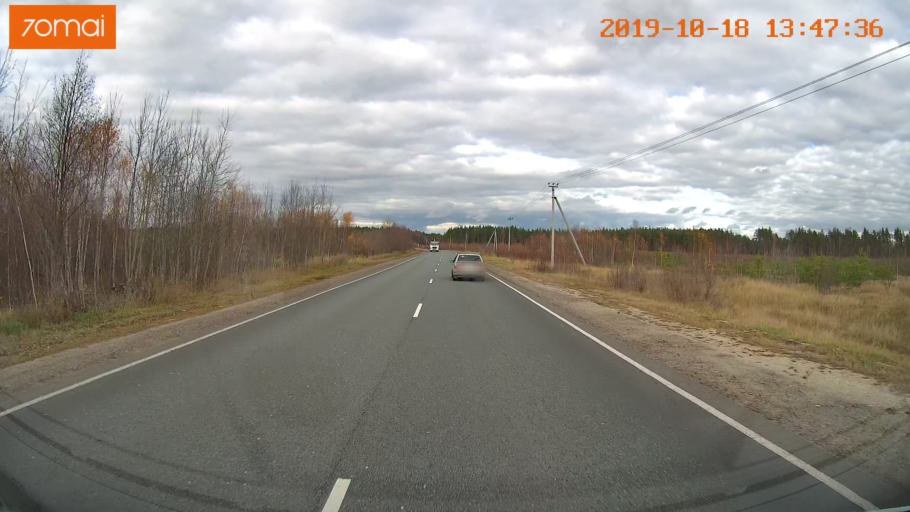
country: RU
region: Moskovskaya
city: Radovitskiy
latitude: 54.9775
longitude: 39.9515
